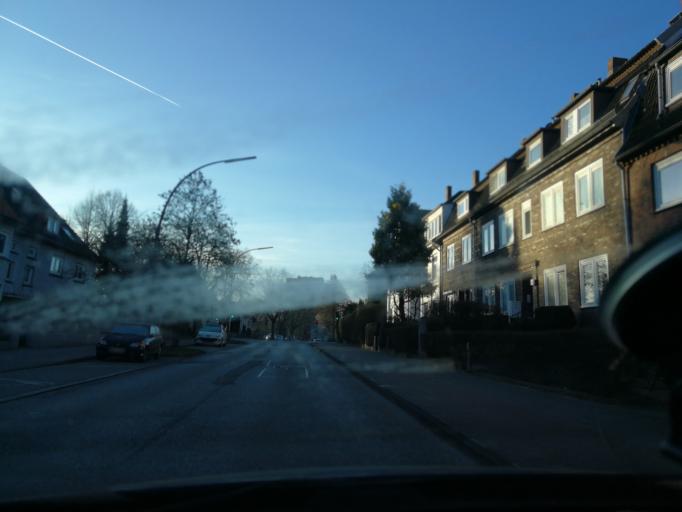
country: DE
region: Hamburg
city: Harburg
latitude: 53.4627
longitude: 9.9570
